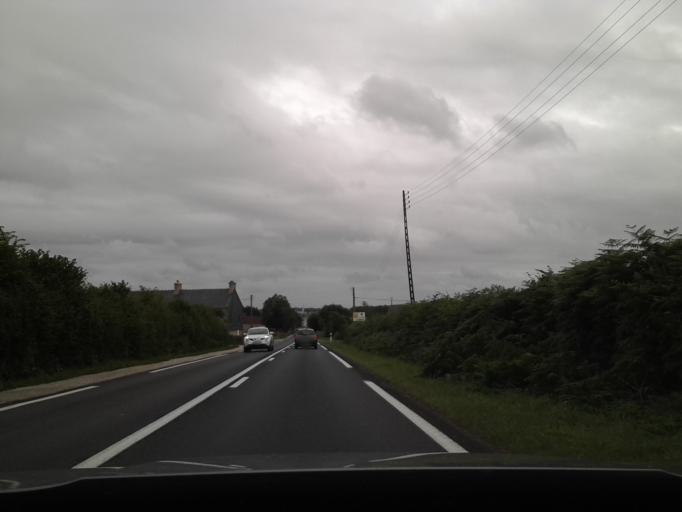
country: FR
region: Lower Normandy
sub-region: Departement de la Manche
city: Valognes
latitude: 49.5188
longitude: -1.4943
